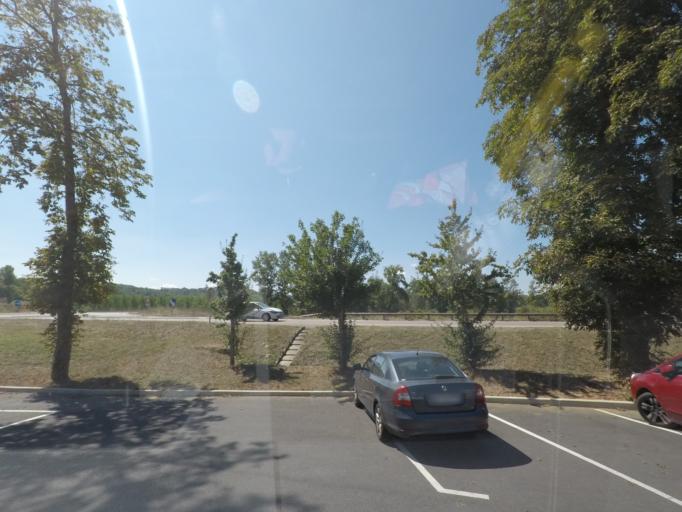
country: FR
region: Midi-Pyrenees
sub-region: Departement du Lot
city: Figeac
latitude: 44.5965
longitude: 1.9750
